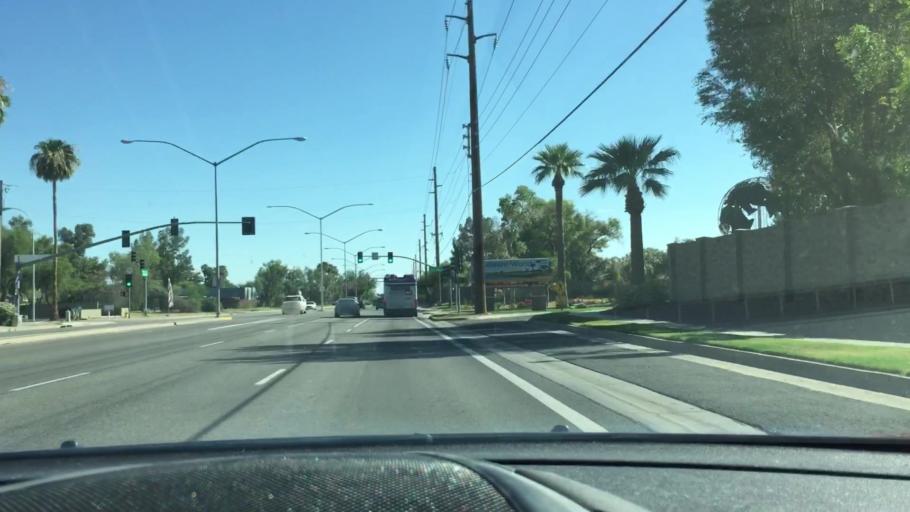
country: US
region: Arizona
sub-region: Maricopa County
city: Gilbert
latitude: 33.3998
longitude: -111.6848
